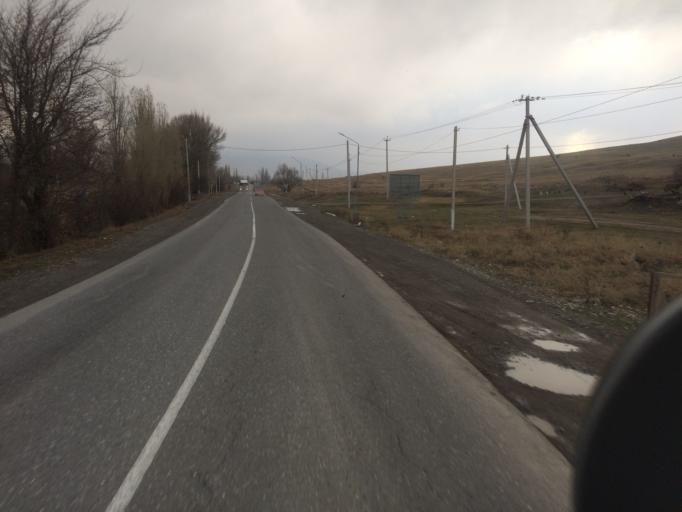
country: KZ
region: Ongtustik Qazaqstan
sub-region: Tulkibas Audany
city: Zhabagly
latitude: 42.5171
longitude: 70.5836
